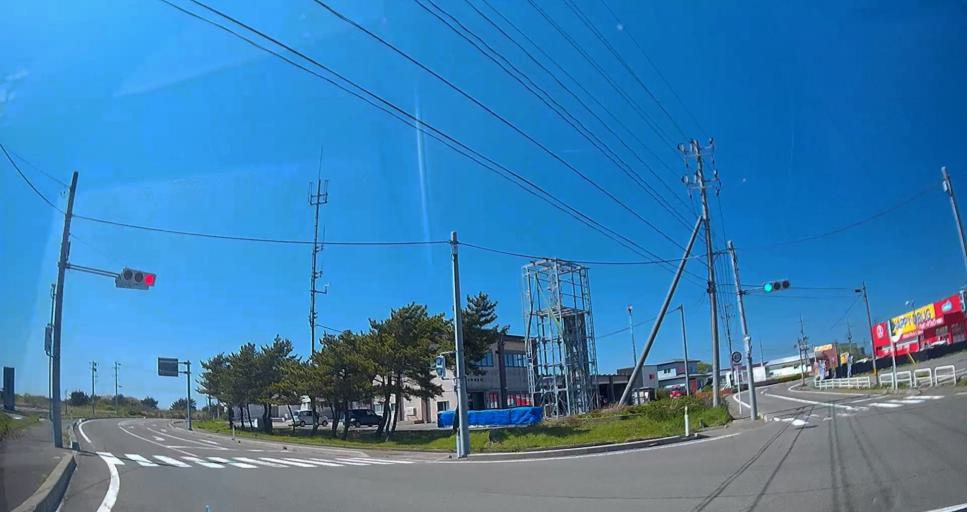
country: JP
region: Hokkaido
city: Hakodate
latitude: 41.5226
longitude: 140.9053
